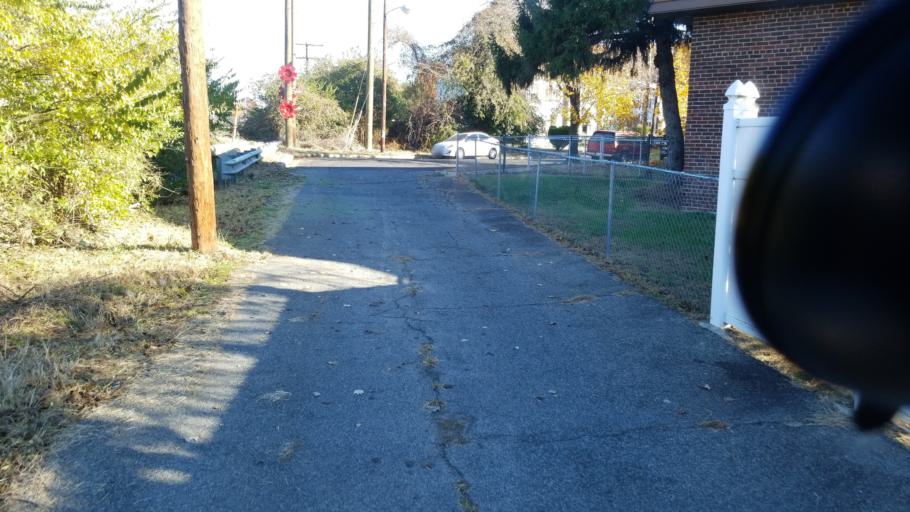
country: US
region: Maryland
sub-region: Prince George's County
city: Coral Hills
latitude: 38.8874
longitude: -76.9590
